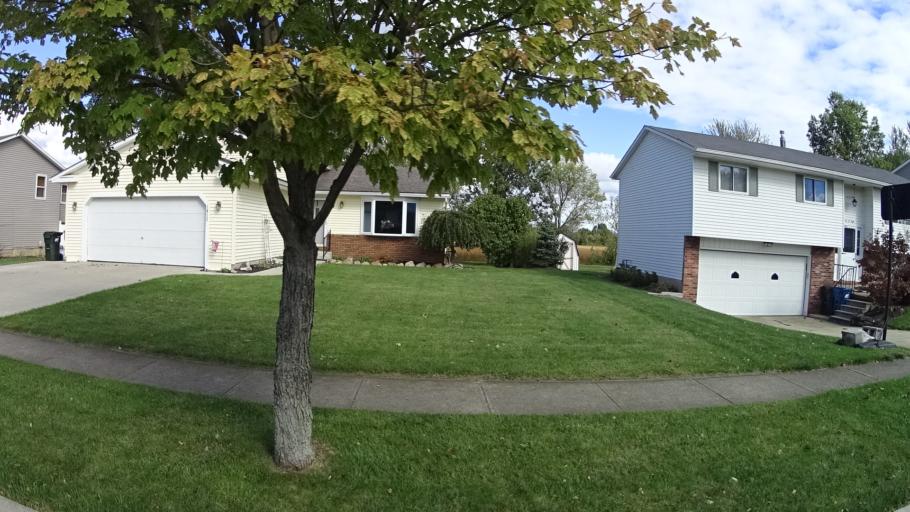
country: US
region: Ohio
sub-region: Lorain County
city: Grafton
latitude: 41.2840
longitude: -82.0564
